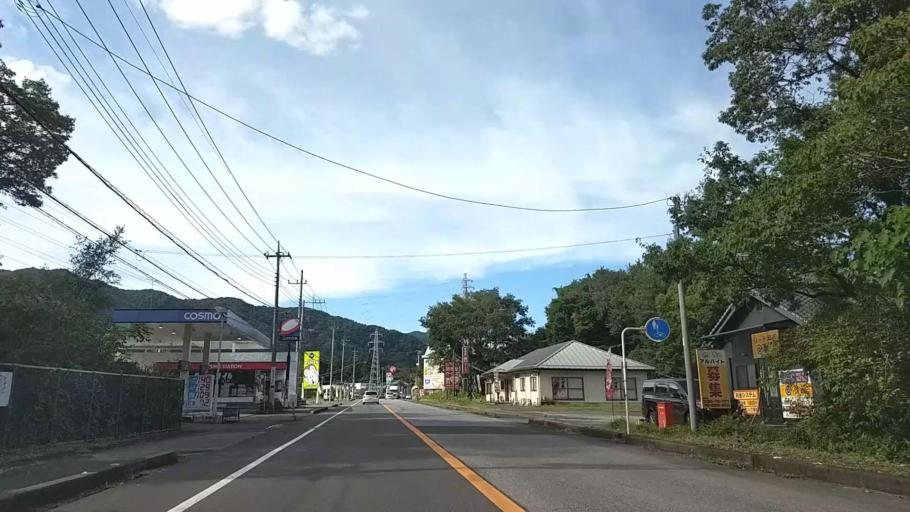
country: JP
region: Tochigi
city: Imaichi
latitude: 36.7822
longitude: 139.7039
